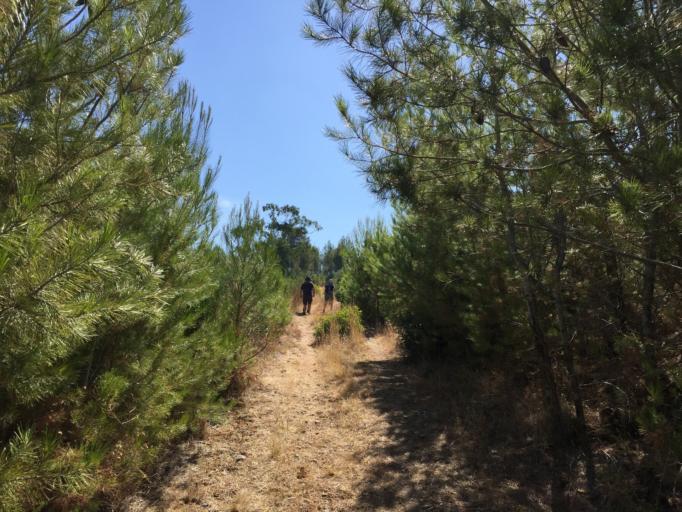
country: PT
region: Lisbon
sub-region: Alenquer
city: Carregado
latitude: 39.0130
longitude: -8.9775
